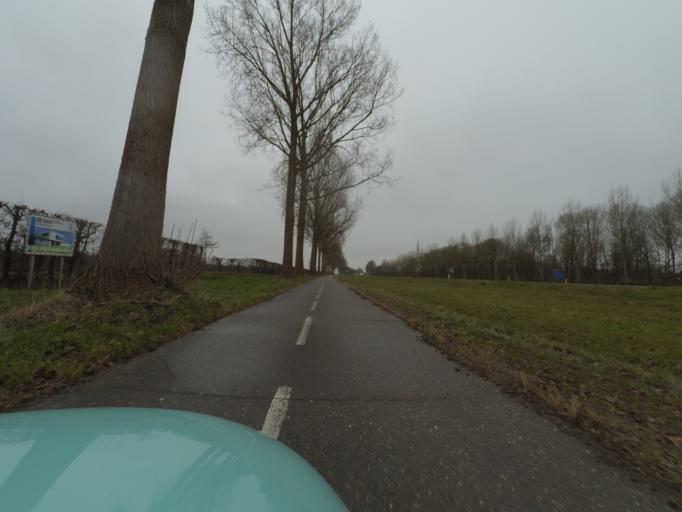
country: NL
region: Flevoland
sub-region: Gemeente Dronten
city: Dronten
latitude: 52.5178
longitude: 5.7338
